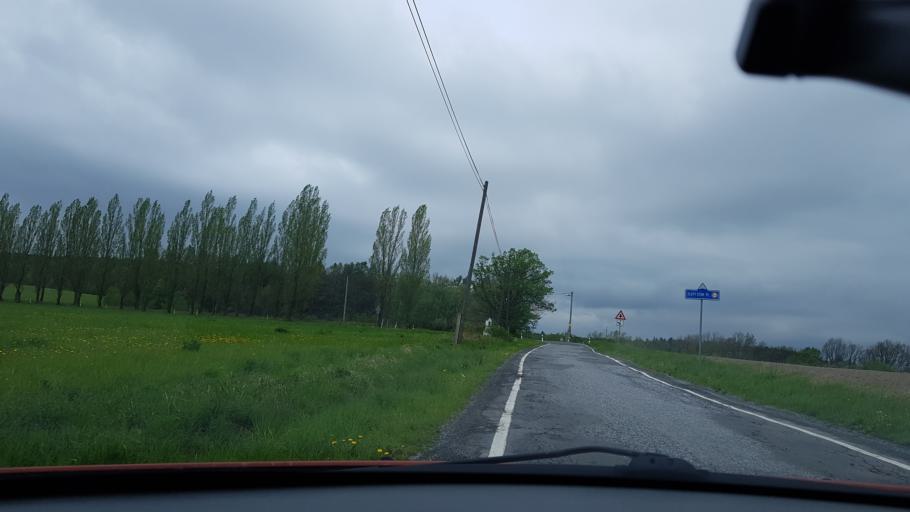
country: PL
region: Lower Silesian Voivodeship
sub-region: Powiat zabkowicki
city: Zloty Stok
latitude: 50.4443
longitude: 16.9007
